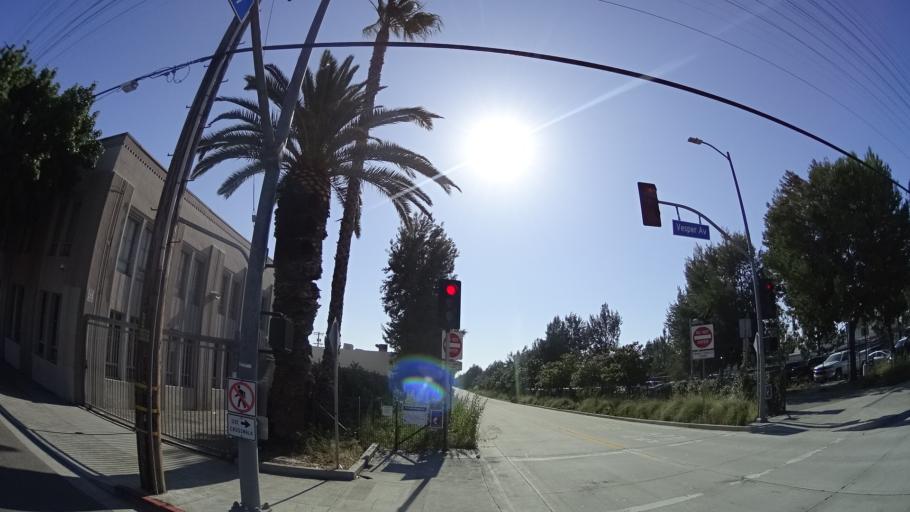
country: US
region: California
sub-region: Los Angeles County
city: Van Nuys
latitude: 34.1805
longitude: -118.4509
